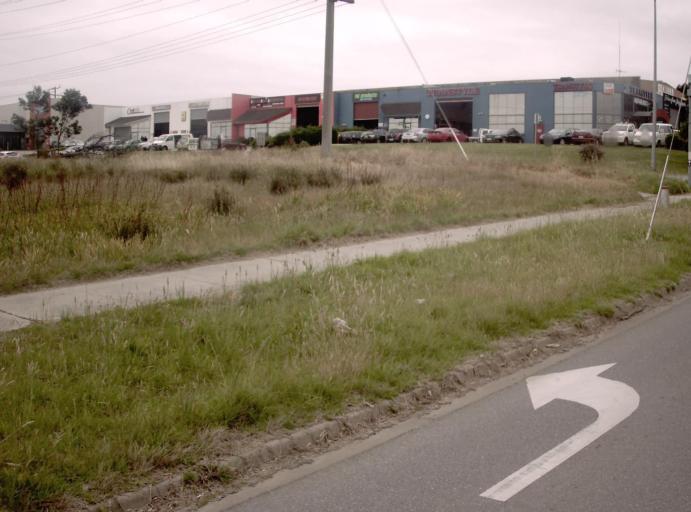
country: AU
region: Victoria
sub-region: Casey
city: Hallam
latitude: -38.0159
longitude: 145.2713
